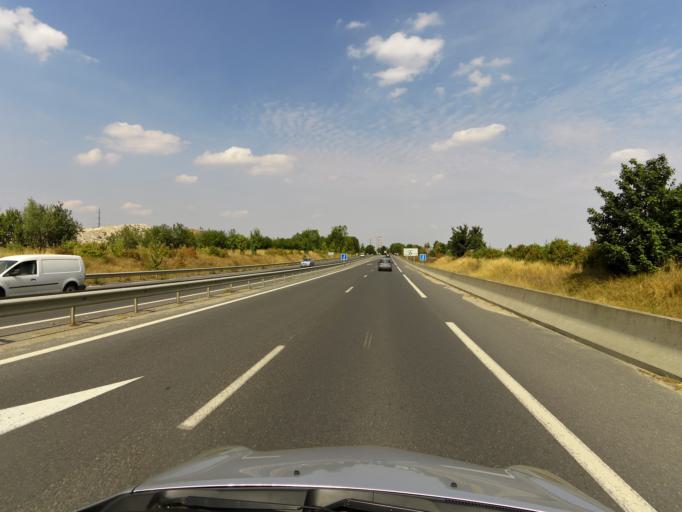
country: FR
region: Champagne-Ardenne
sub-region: Departement de la Marne
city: Bezannes
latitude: 49.2093
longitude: 4.0127
